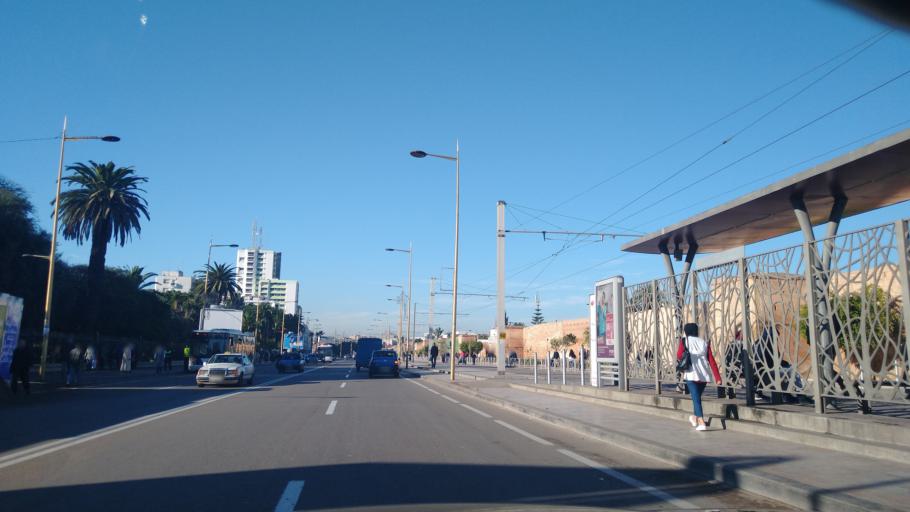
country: MA
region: Rabat-Sale-Zemmour-Zaer
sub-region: Rabat
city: Rabat
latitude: 34.0236
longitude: -6.8340
